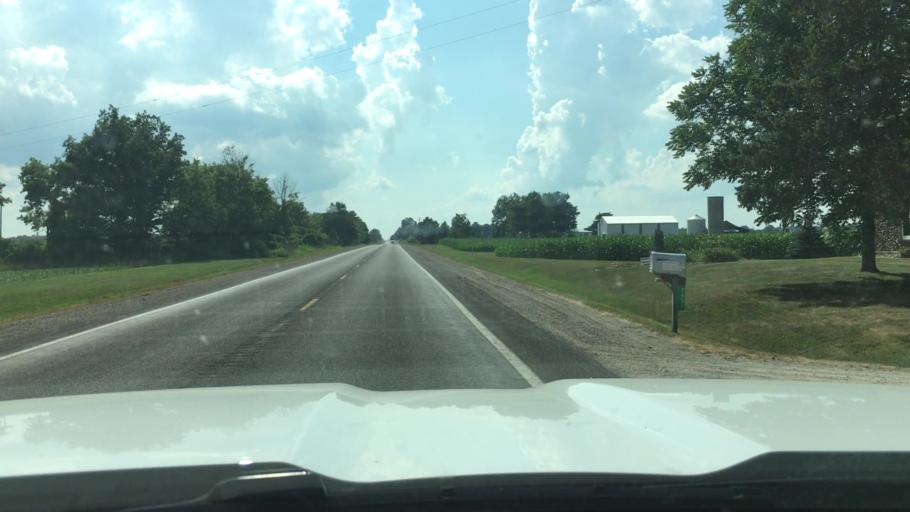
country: US
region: Michigan
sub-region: Montcalm County
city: Carson City
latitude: 43.1775
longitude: -84.9271
